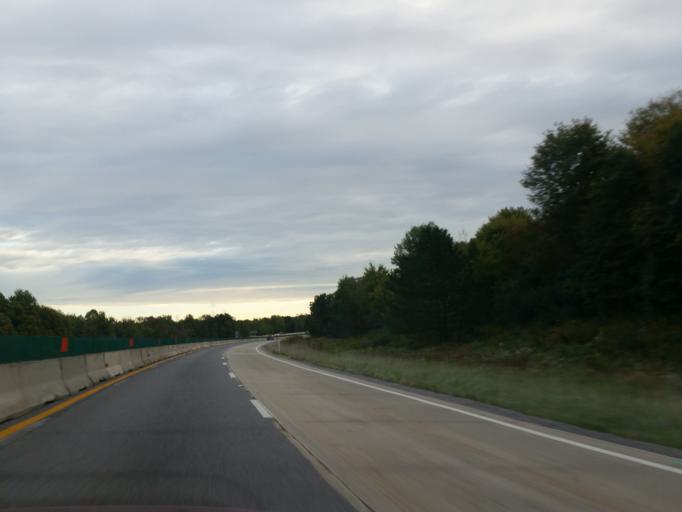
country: US
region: Ohio
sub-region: Ashtabula County
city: Ashtabula
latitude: 41.8245
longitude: -80.7943
